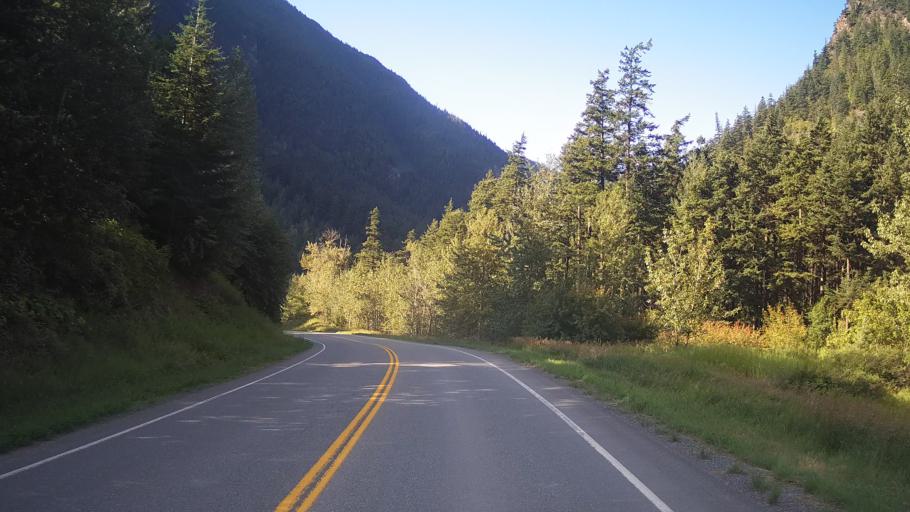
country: CA
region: British Columbia
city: Lillooet
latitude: 50.5639
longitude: -122.0909
